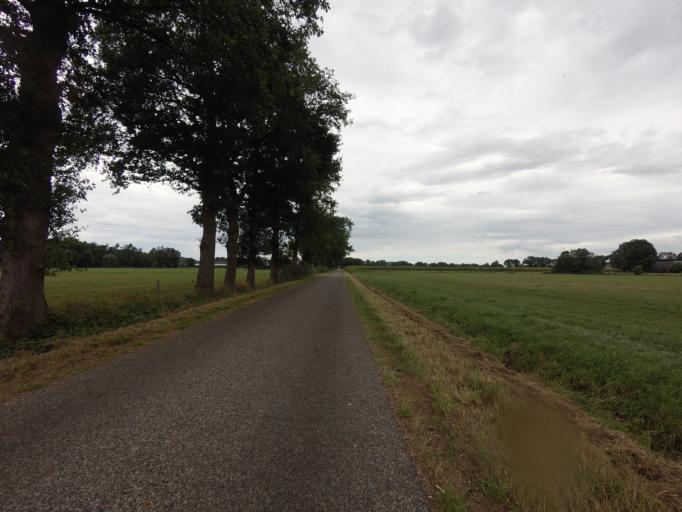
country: NL
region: Overijssel
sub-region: Gemeente Raalte
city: Raalte
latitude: 52.3588
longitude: 6.3653
